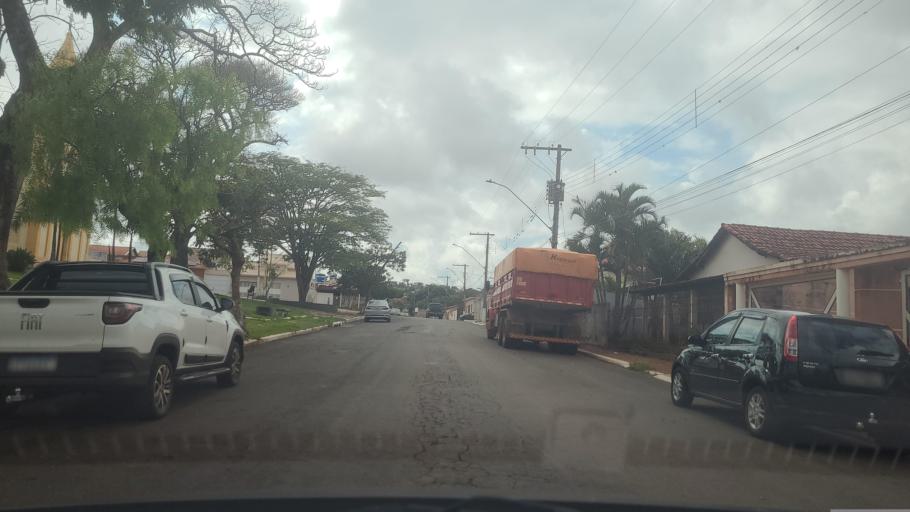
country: BR
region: Minas Gerais
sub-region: Carmo Do Paranaiba
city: Carmo do Paranaiba
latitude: -19.1941
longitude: -46.2478
